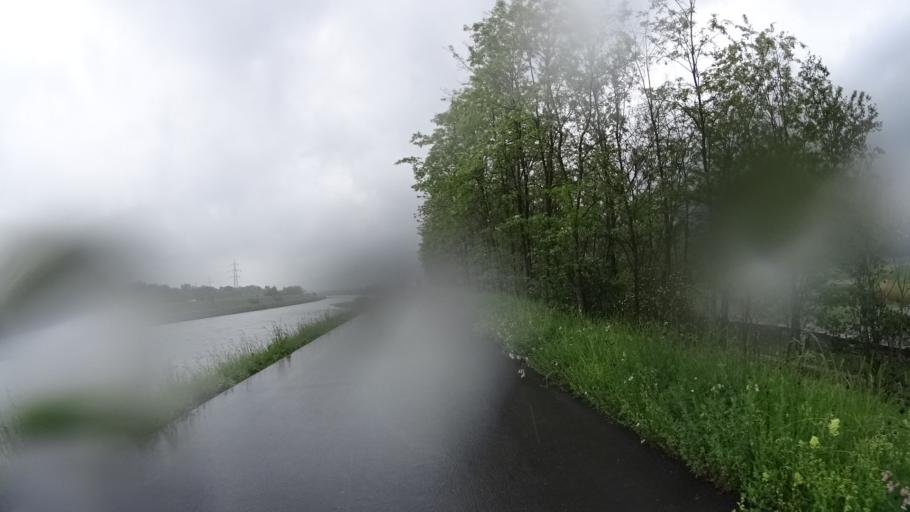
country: LI
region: Triesen
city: Triesen
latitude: 47.0887
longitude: 9.5171
